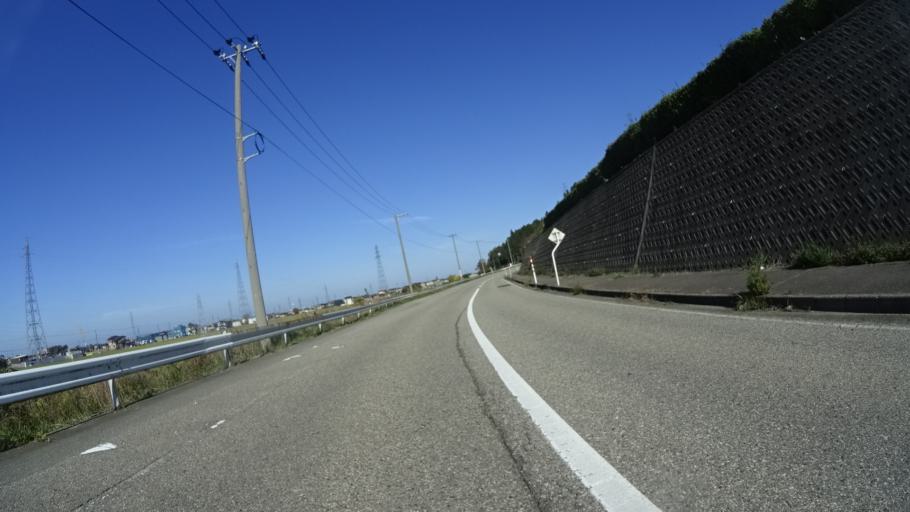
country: JP
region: Ishikawa
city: Tsurugi-asahimachi
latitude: 36.4768
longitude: 136.6159
